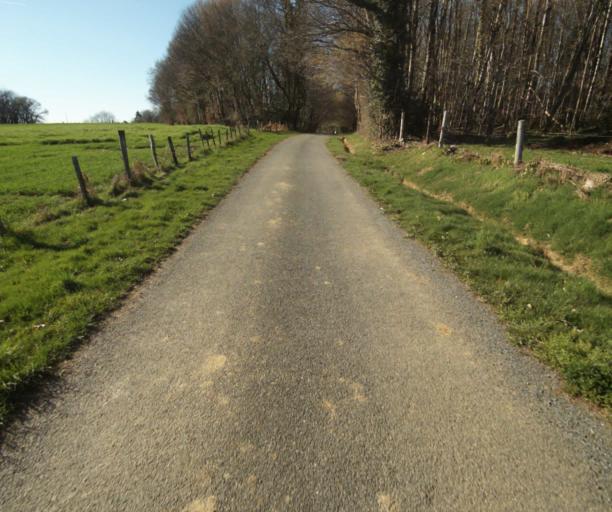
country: FR
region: Limousin
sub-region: Departement de la Correze
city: Chamboulive
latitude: 45.3995
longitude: 1.6666
